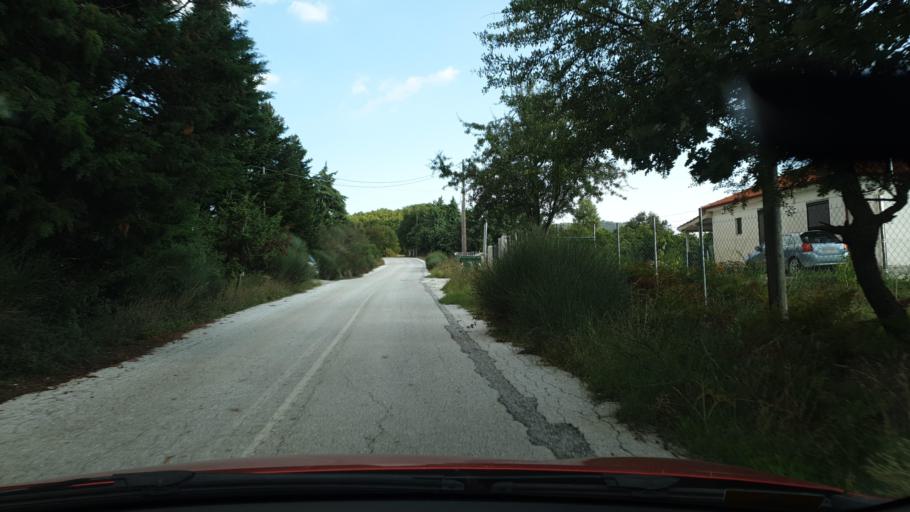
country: GR
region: Central Macedonia
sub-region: Nomos Thessalonikis
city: Peristera
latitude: 40.5192
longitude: 23.2094
